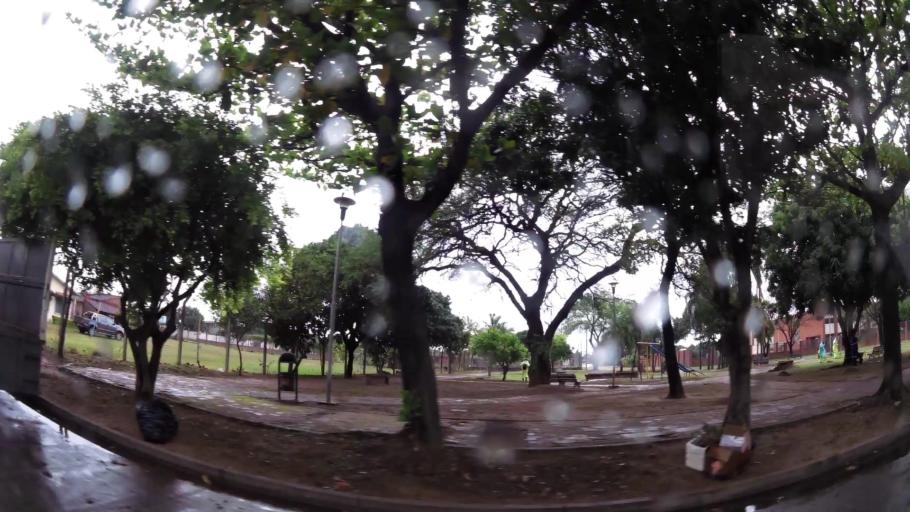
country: BO
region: Santa Cruz
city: Santa Cruz de la Sierra
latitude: -17.7940
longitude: -63.1514
